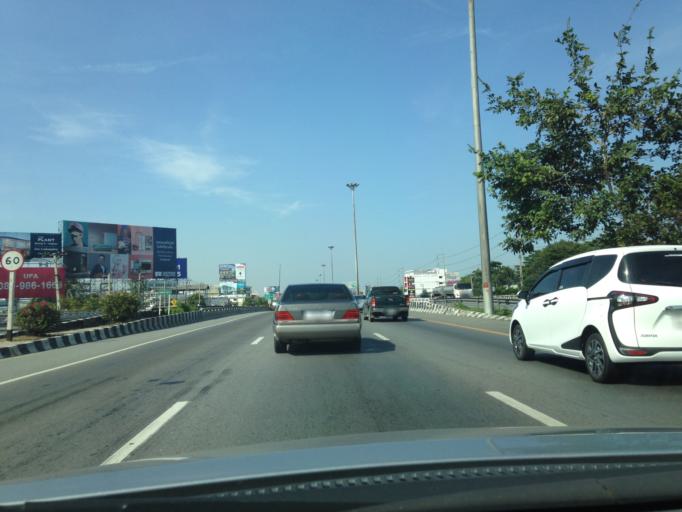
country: TH
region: Nonthaburi
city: Bang Yai
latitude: 13.8393
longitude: 100.4131
